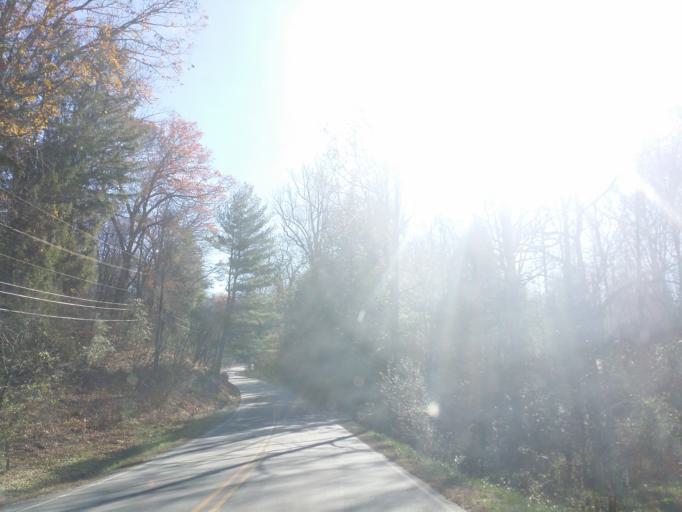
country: US
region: North Carolina
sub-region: Buncombe County
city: Swannanoa
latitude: 35.6008
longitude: -82.4427
